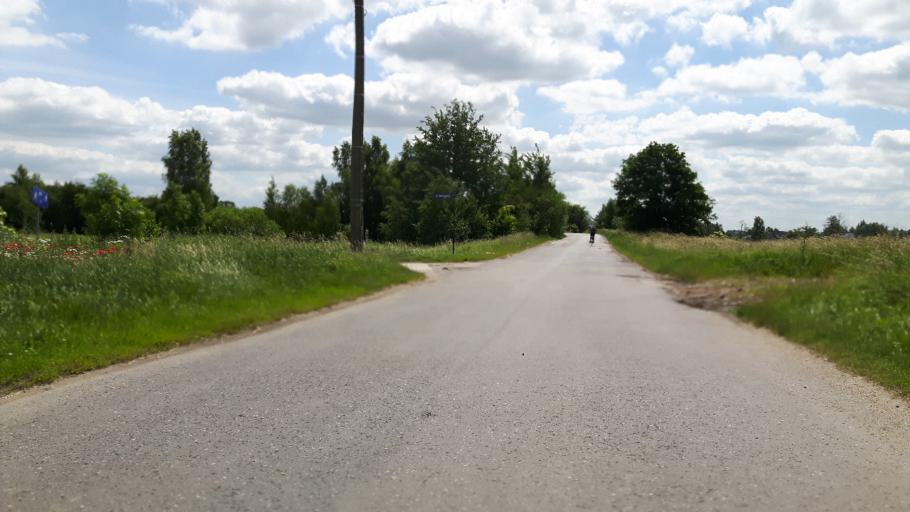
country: PL
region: Pomeranian Voivodeship
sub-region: Powiat gdanski
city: Cedry Wielkie
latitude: 54.3420
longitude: 18.7944
